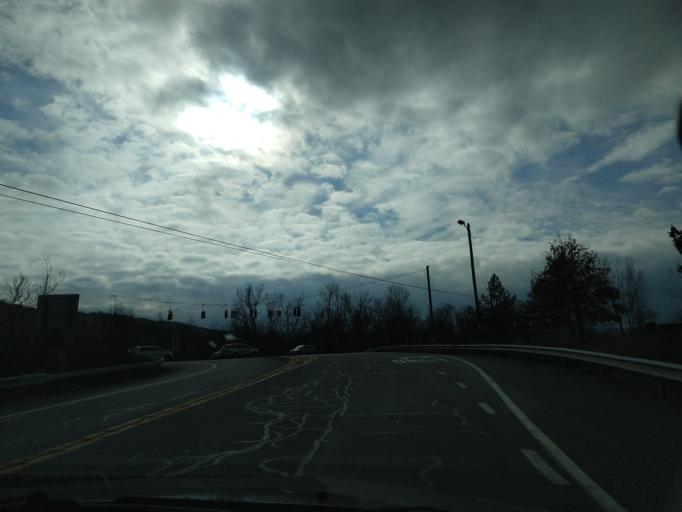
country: US
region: New York
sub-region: Tompkins County
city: South Hill
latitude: 42.4151
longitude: -76.5314
